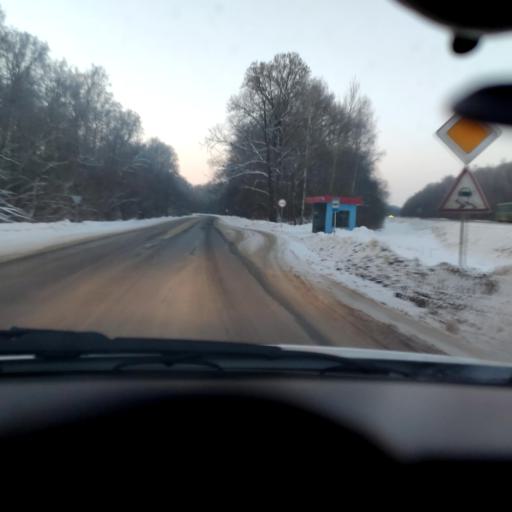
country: RU
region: Kursk
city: Zheleznogorsk
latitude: 52.2878
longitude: 35.3232
